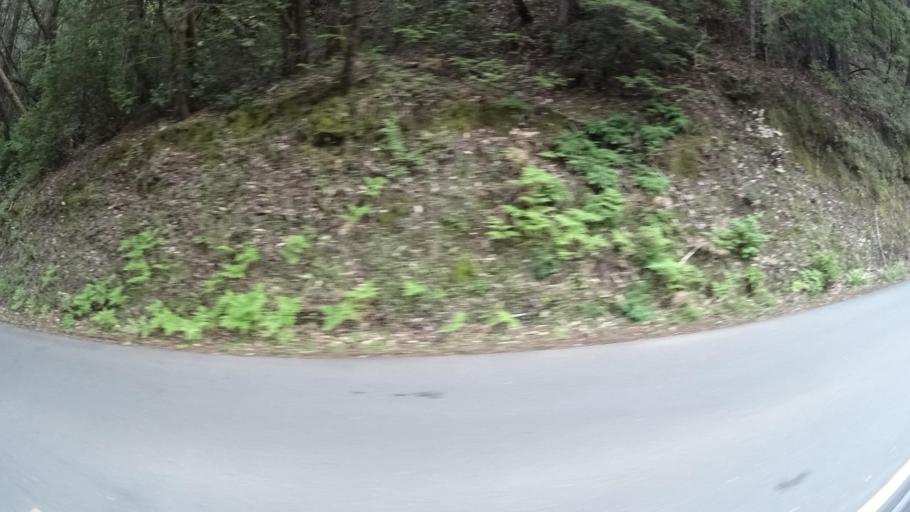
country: US
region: California
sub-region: Humboldt County
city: Redway
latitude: 40.2807
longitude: -123.8488
